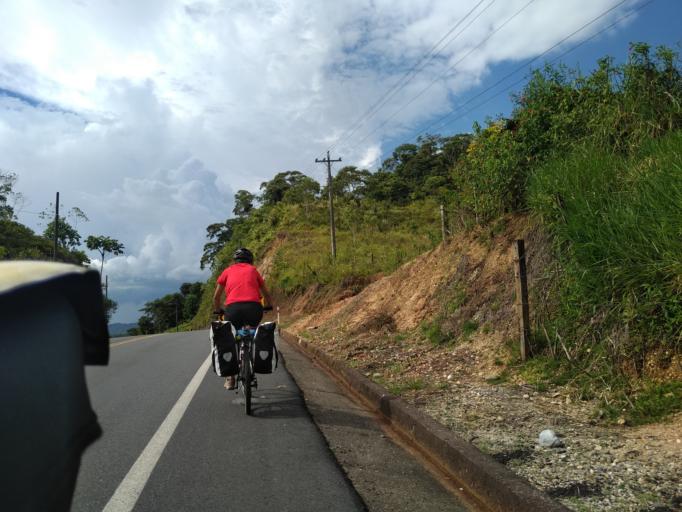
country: EC
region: Napo
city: Tena
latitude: -1.0801
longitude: -77.7914
